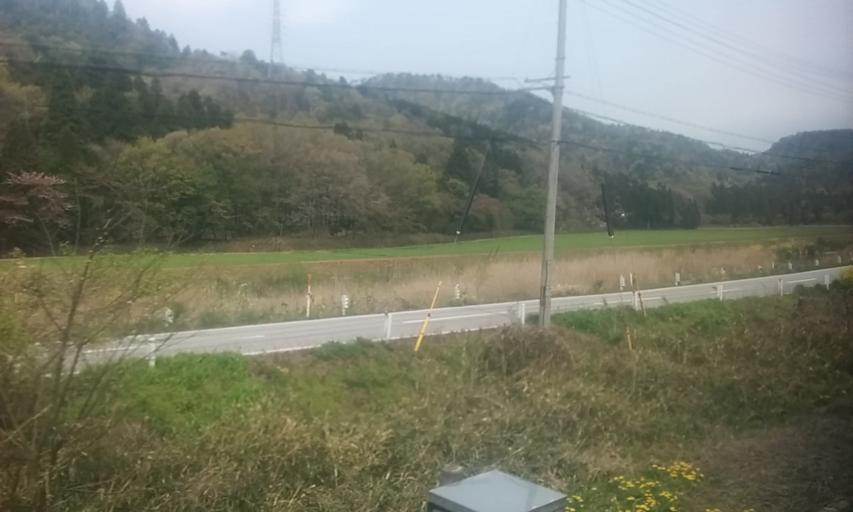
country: JP
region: Shiga Prefecture
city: Nagahama
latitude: 35.3434
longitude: 136.3631
